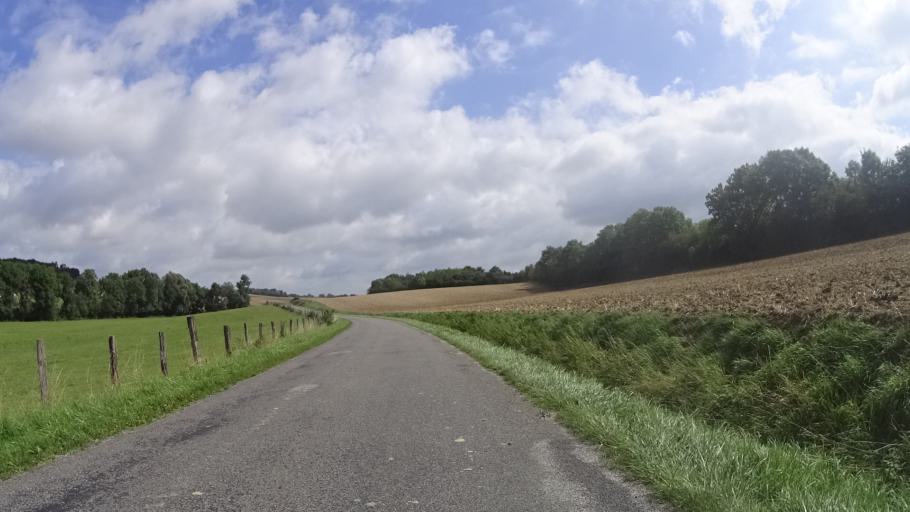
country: FR
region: Lorraine
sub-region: Departement de la Meuse
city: Ligny-en-Barrois
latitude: 48.7308
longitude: 5.3768
